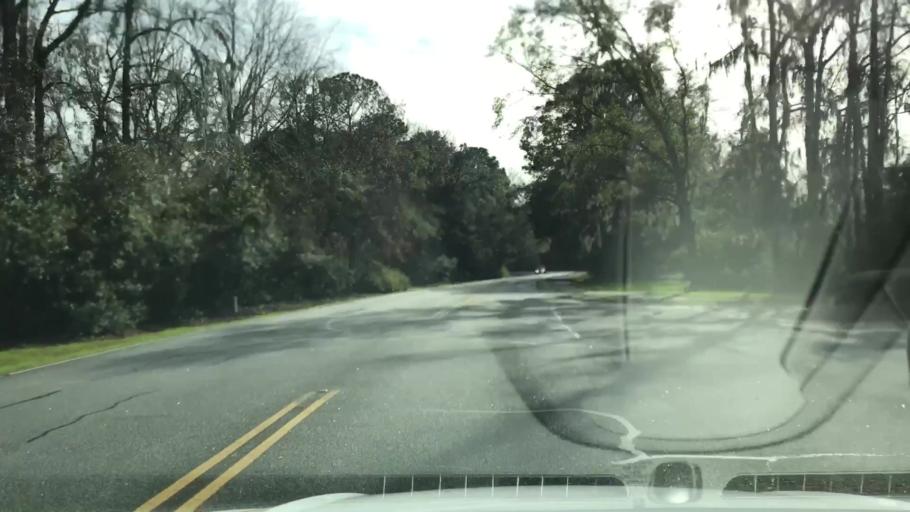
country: US
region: South Carolina
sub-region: Beaufort County
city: Hilton Head Island
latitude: 32.2223
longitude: -80.7231
